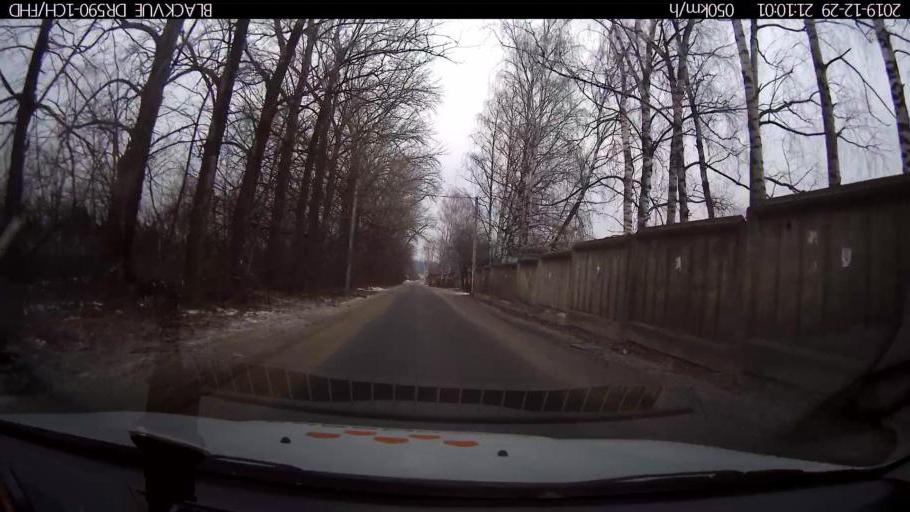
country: RU
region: Nizjnij Novgorod
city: Afonino
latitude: 56.2198
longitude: 44.0373
